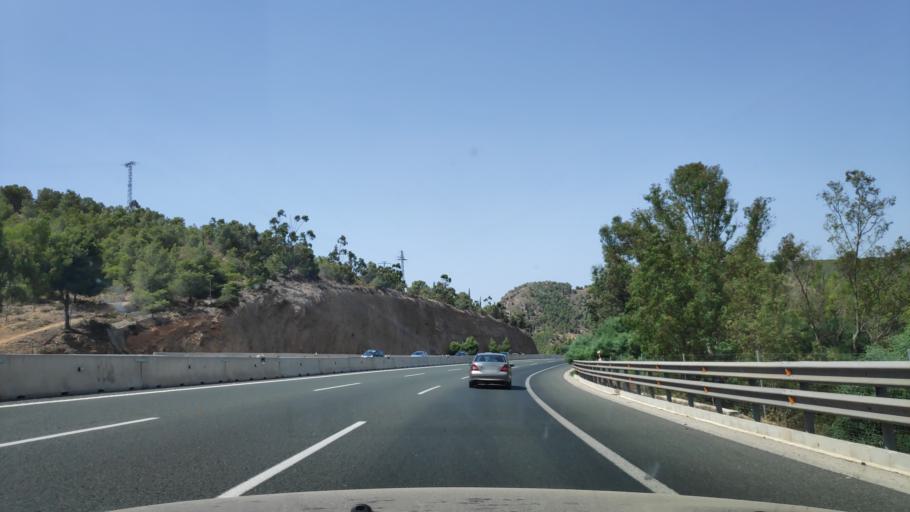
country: ES
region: Murcia
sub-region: Murcia
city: Murcia
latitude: 37.8929
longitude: -1.1425
